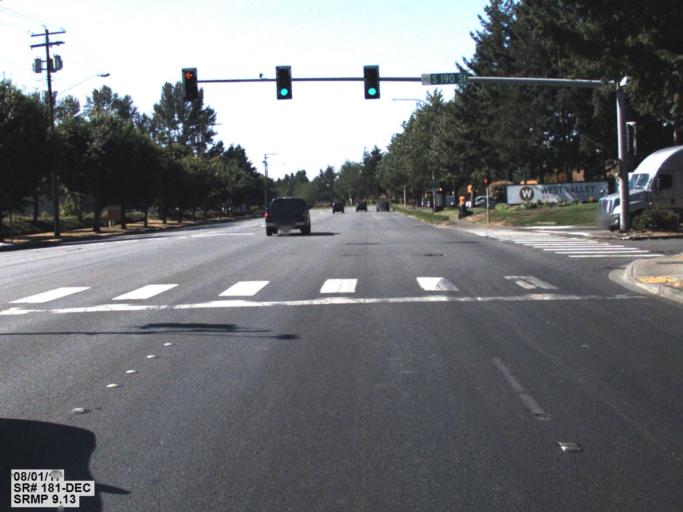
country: US
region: Washington
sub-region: King County
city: Tukwila
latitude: 47.4327
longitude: -122.2487
